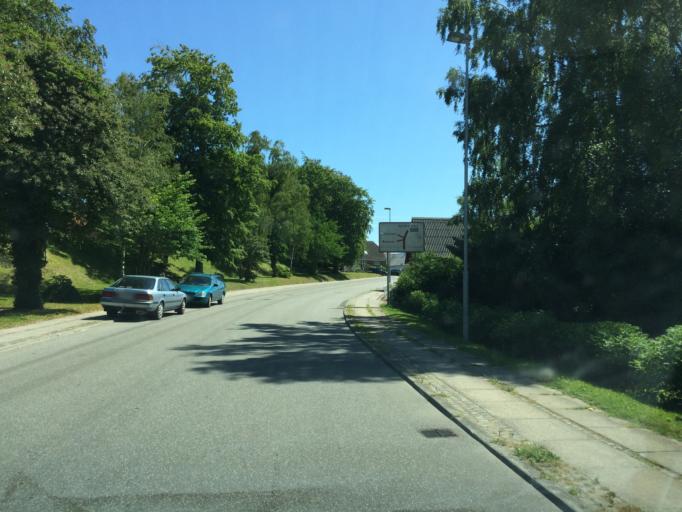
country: DK
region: Central Jutland
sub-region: Samso Kommune
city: Tranebjerg
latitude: 55.8310
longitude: 10.5897
